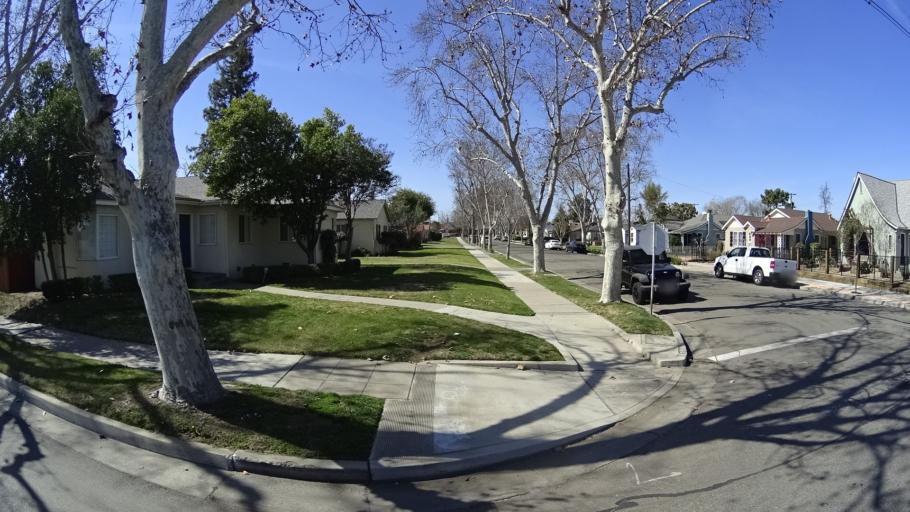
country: US
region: California
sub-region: Fresno County
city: Fresno
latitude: 36.7676
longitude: -119.8087
